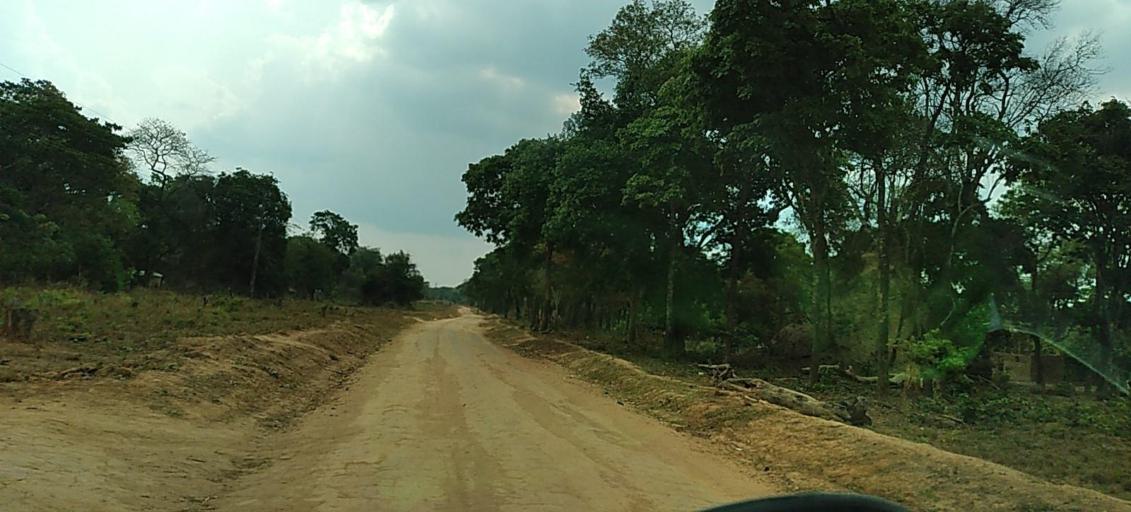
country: ZM
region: North-Western
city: Solwezi
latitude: -12.7849
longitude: 26.5107
